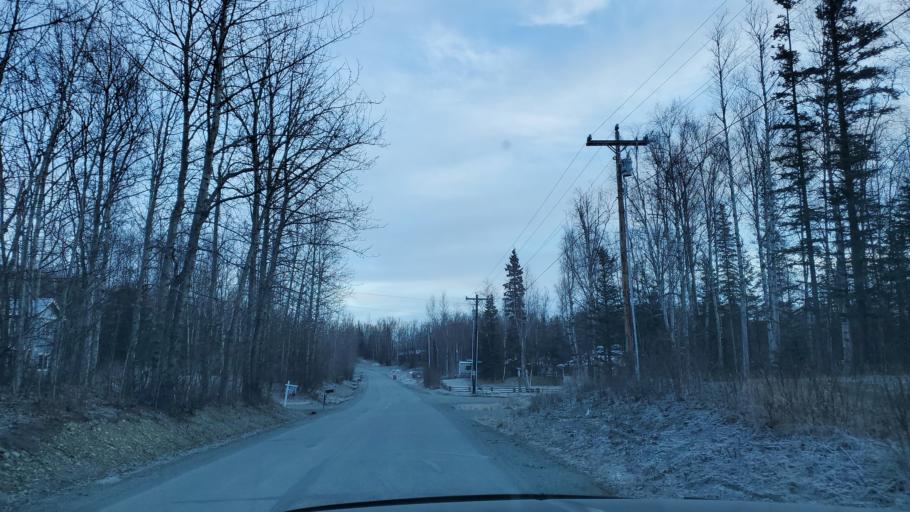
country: US
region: Alaska
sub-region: Matanuska-Susitna Borough
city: Lakes
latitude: 61.6037
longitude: -149.3205
